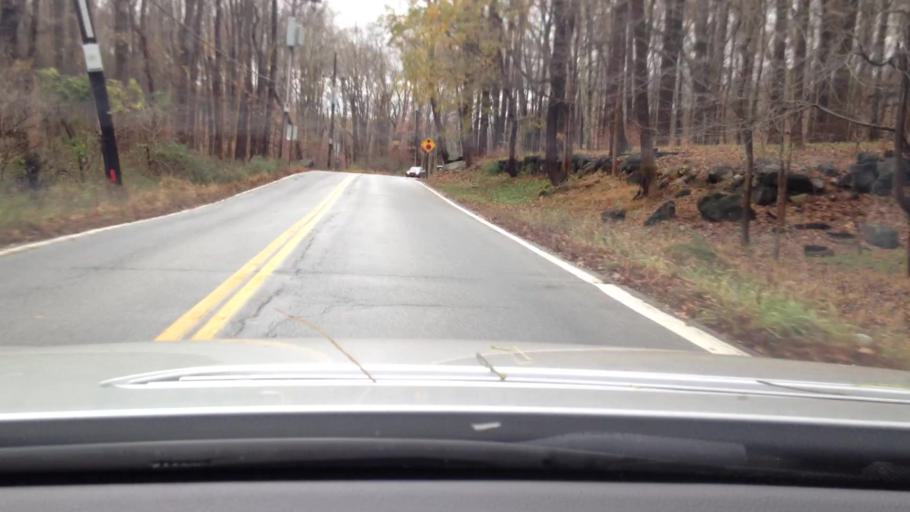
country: US
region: New York
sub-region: Westchester County
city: Croton-on-Hudson
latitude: 41.2357
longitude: -73.8942
